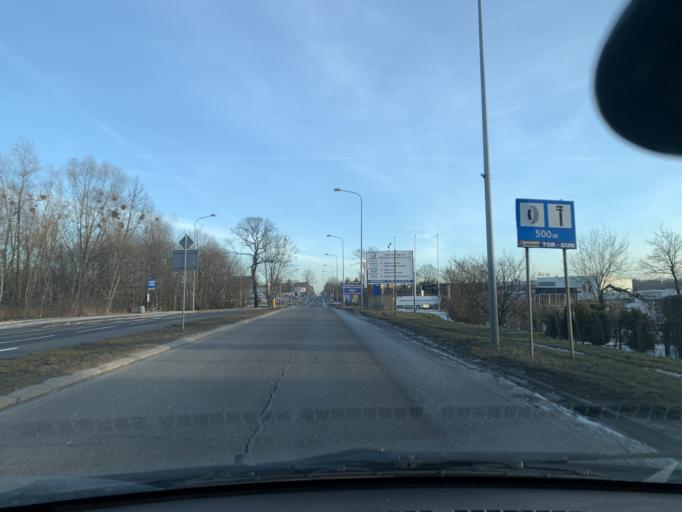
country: PL
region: Silesian Voivodeship
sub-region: Piekary Slaskie
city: Piekary Slaskie
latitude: 50.3615
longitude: 18.9033
